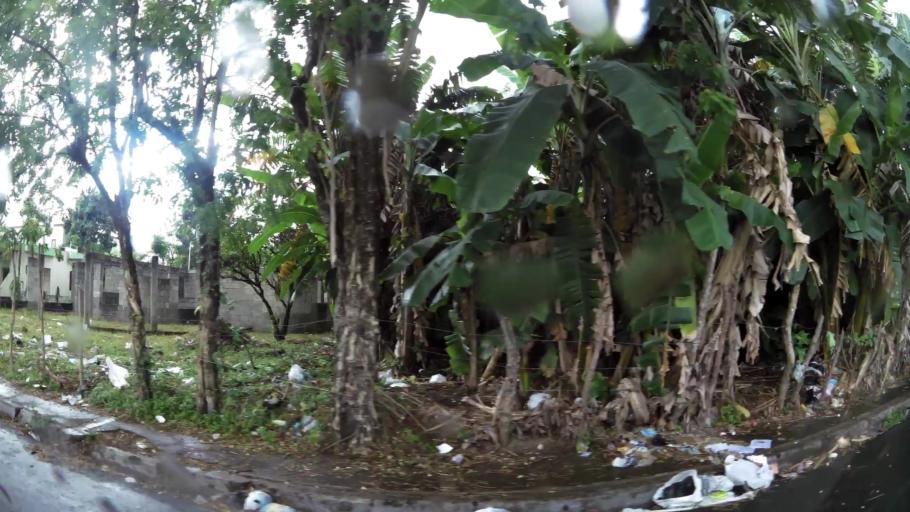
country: DO
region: Monsenor Nouel
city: Bonao
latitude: 18.9356
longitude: -70.3989
